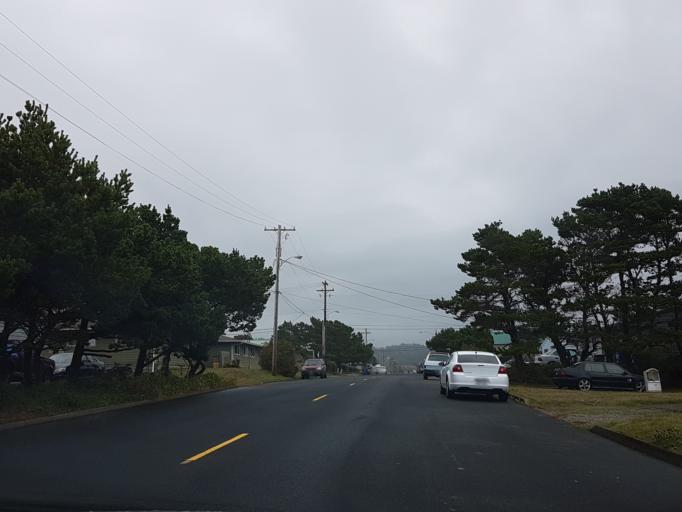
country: US
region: Oregon
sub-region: Lincoln County
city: Newport
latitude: 44.6447
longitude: -124.0581
